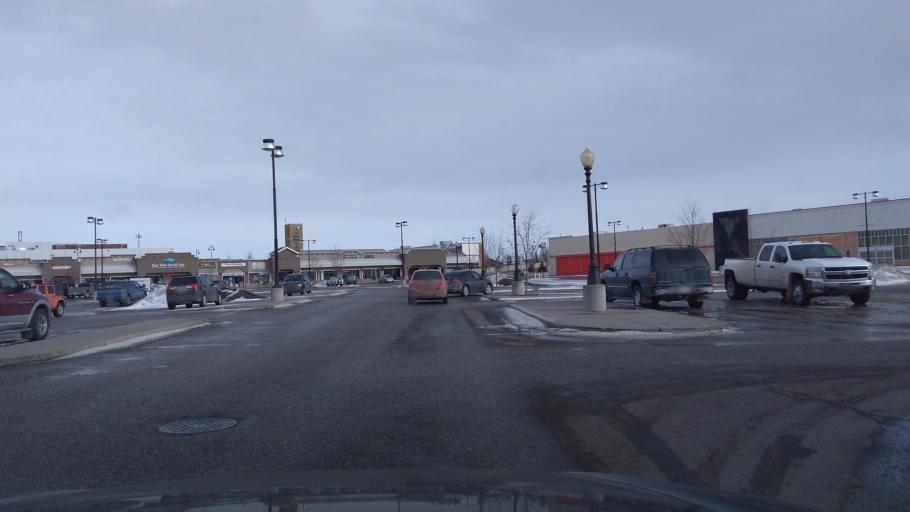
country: CA
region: Alberta
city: Cochrane
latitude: 51.1847
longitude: -114.4773
